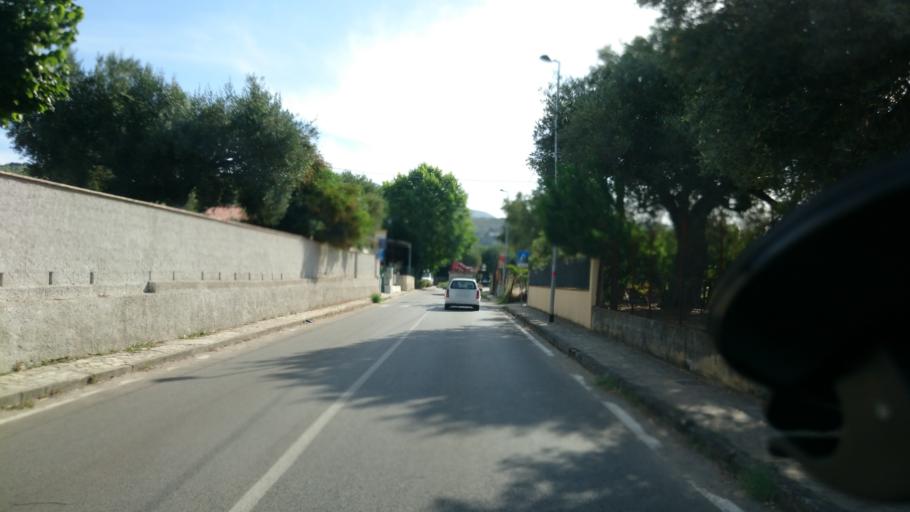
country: IT
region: Campania
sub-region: Provincia di Salerno
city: Marina di Camerota
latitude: 40.0014
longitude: 15.3596
